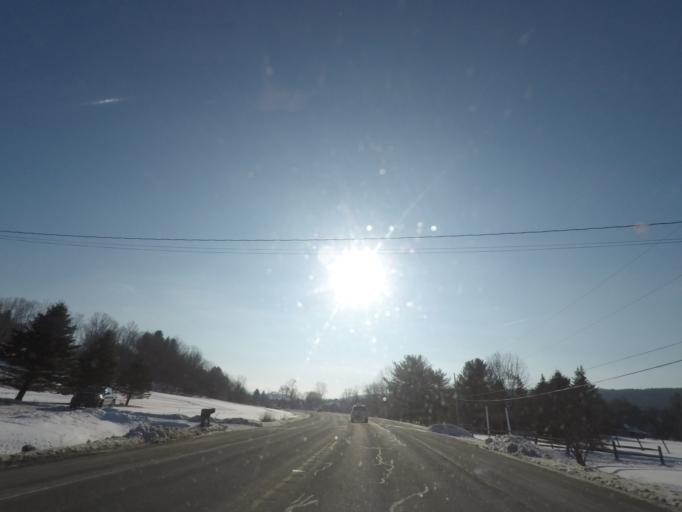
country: US
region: Massachusetts
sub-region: Berkshire County
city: Pittsfield
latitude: 42.5152
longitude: -73.3636
